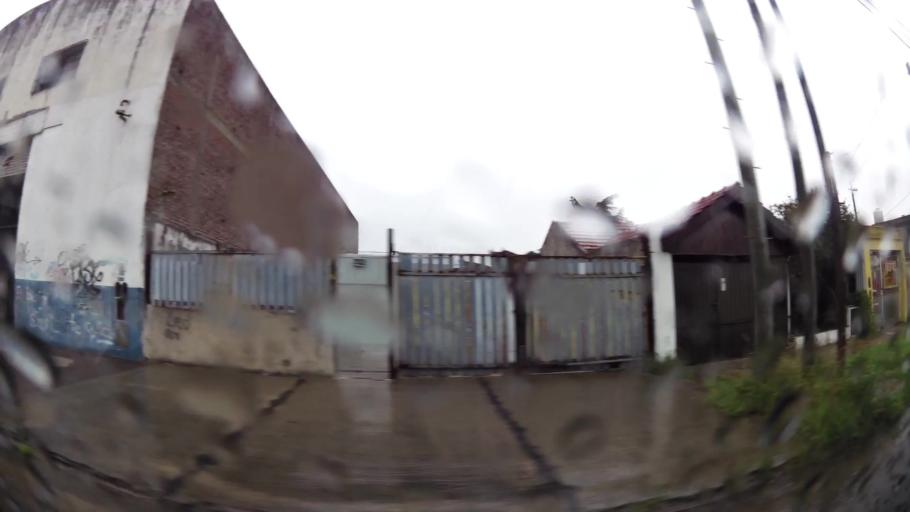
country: AR
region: Buenos Aires
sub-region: Partido de Lanus
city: Lanus
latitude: -34.7010
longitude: -58.4087
